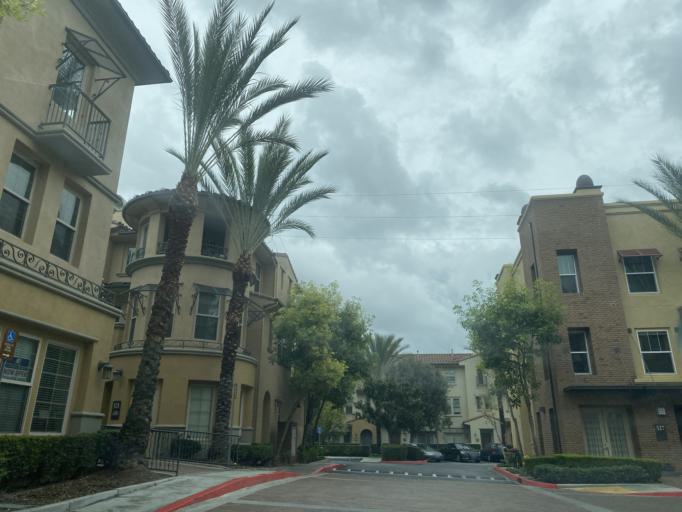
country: US
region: California
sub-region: Orange County
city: Fullerton
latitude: 33.8678
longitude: -117.9223
